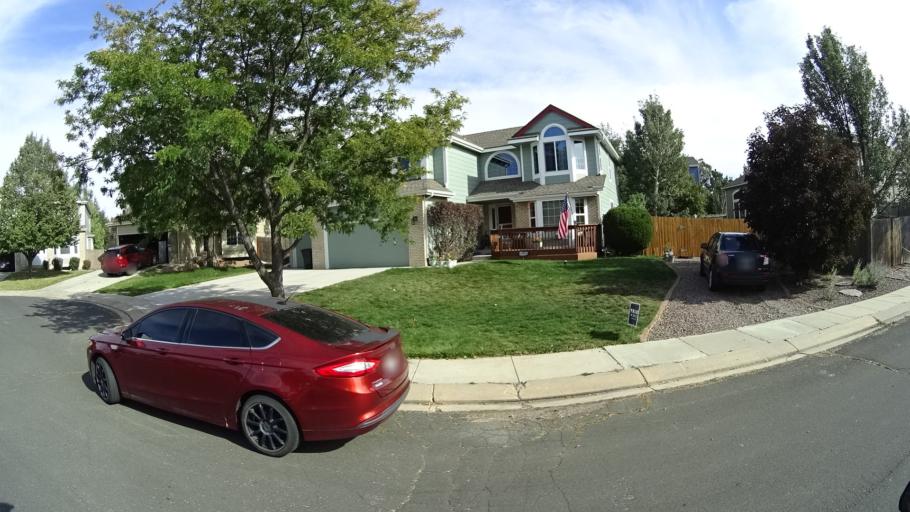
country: US
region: Colorado
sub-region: El Paso County
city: Cimarron Hills
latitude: 38.9032
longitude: -104.6920
